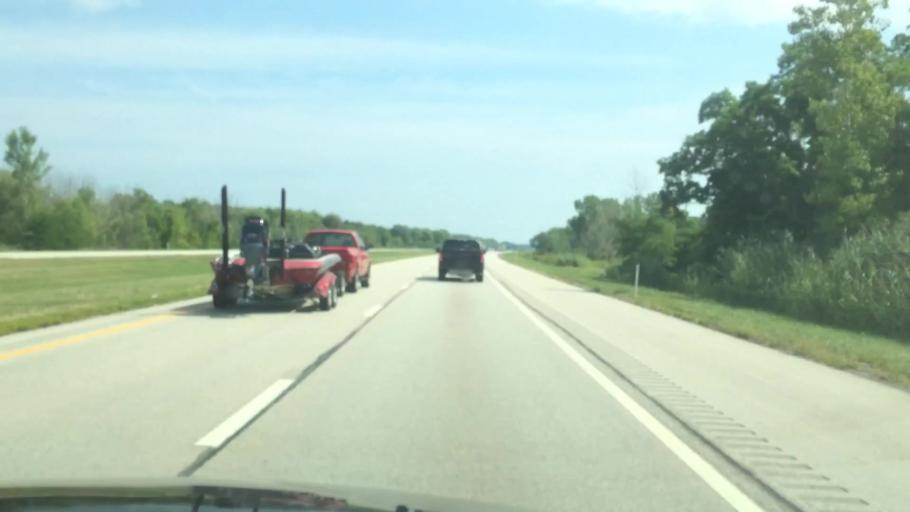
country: US
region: Ohio
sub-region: Ashtabula County
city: Conneaut
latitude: 41.9085
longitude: -80.6017
